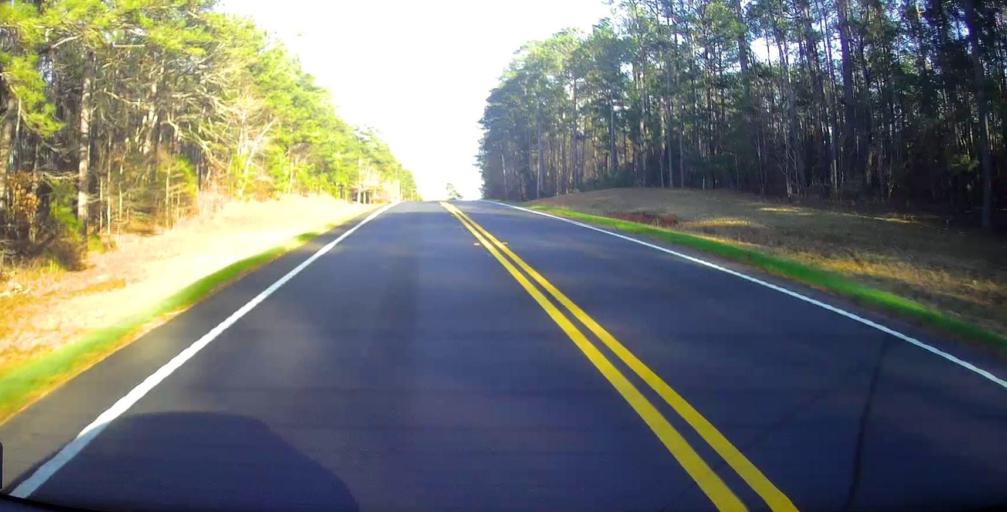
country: US
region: Georgia
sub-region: Harris County
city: Hamilton
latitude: 32.7407
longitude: -84.9695
